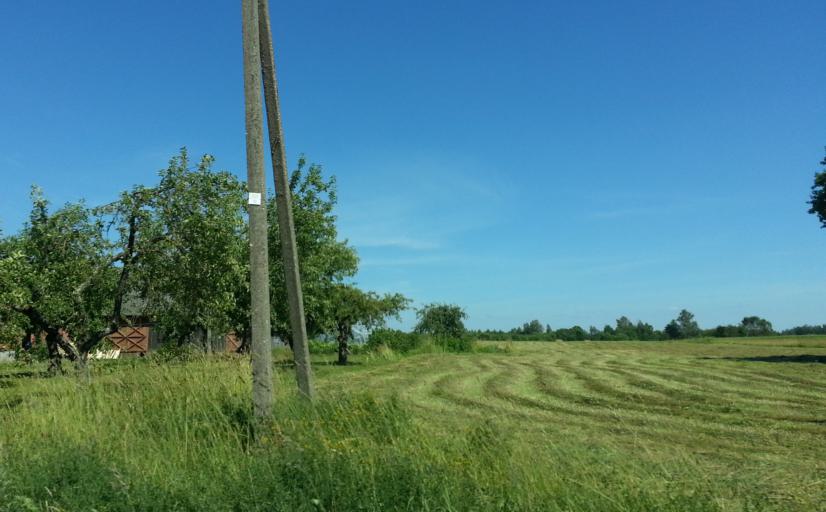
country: LT
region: Panevezys
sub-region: Birzai
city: Birzai
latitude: 56.2438
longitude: 24.6928
